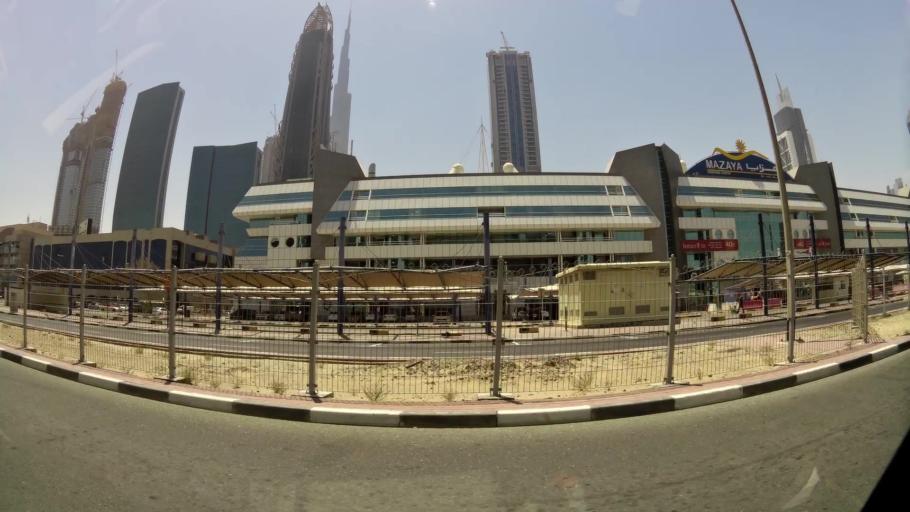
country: AE
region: Dubai
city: Dubai
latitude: 25.1999
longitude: 55.2649
